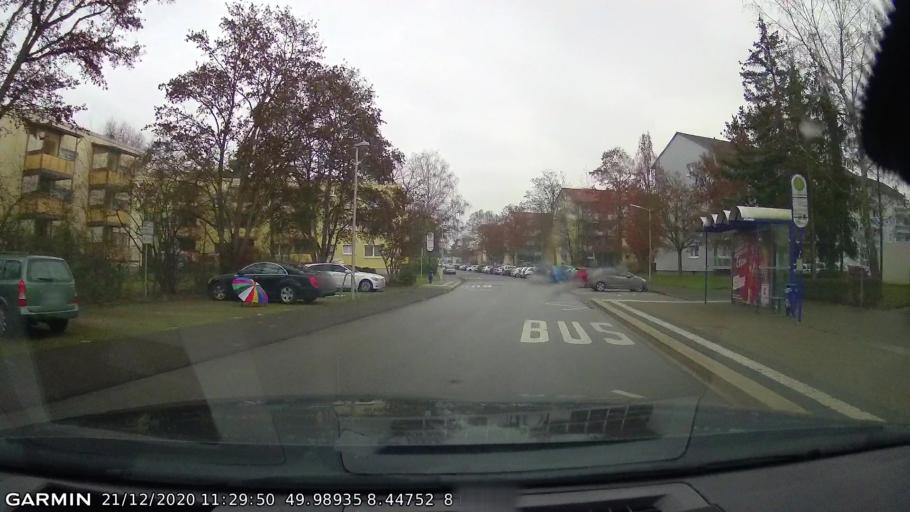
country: DE
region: Hesse
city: Raunheim
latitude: 49.9896
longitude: 8.4486
